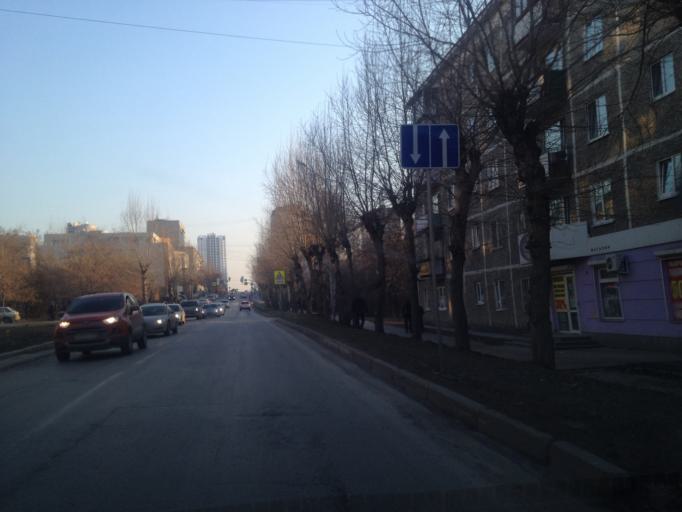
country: RU
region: Sverdlovsk
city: Yekaterinburg
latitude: 56.8300
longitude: 60.5516
